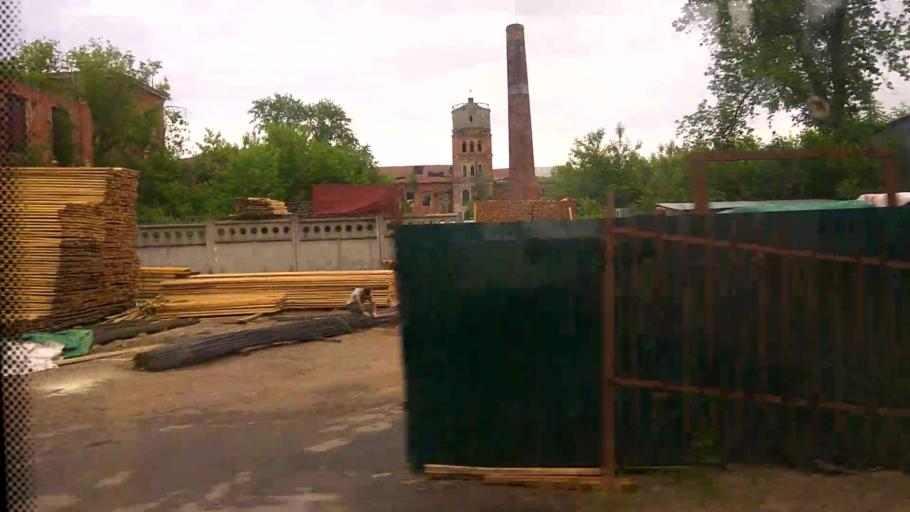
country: RU
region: Moskovskaya
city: Ozery
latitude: 54.8521
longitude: 38.5696
